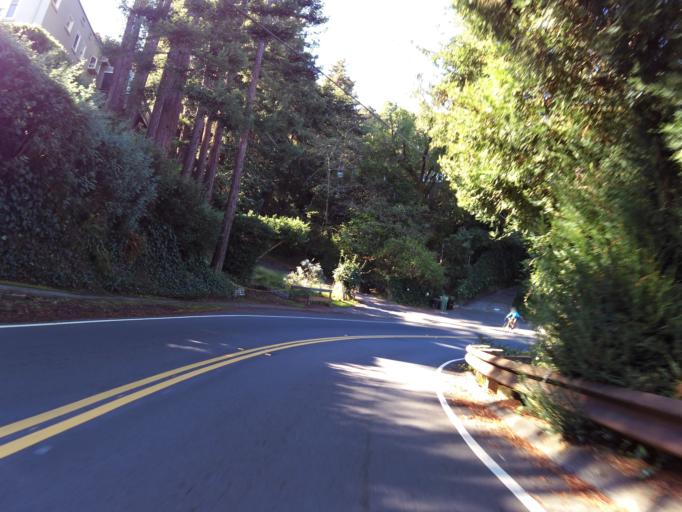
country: US
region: California
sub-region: Marin County
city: Corte Madera
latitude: 37.9224
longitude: -122.5306
